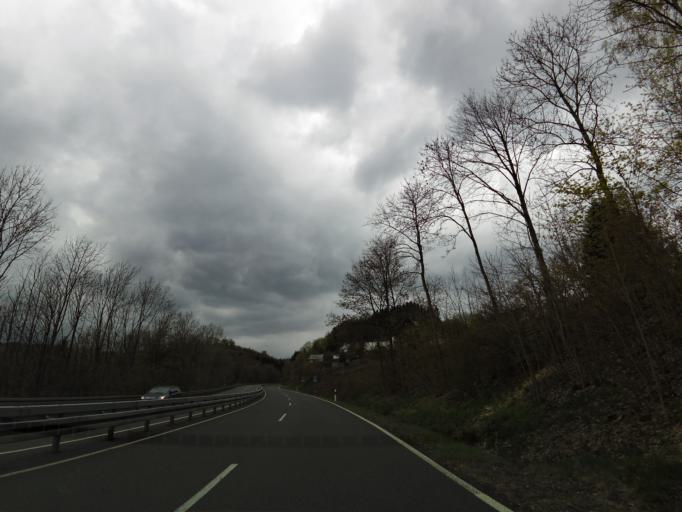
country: DE
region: Lower Saxony
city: Osterode am Harz
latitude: 51.7500
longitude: 10.2873
